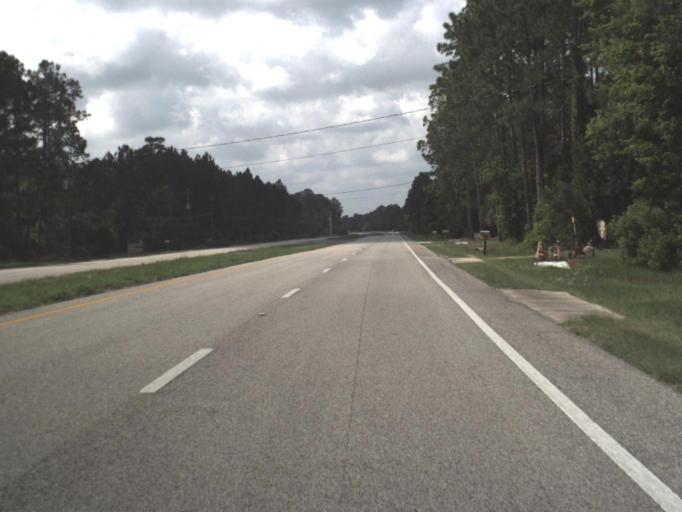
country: US
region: Florida
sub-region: Saint Johns County
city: Butler Beach
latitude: 29.6893
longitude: -81.2945
